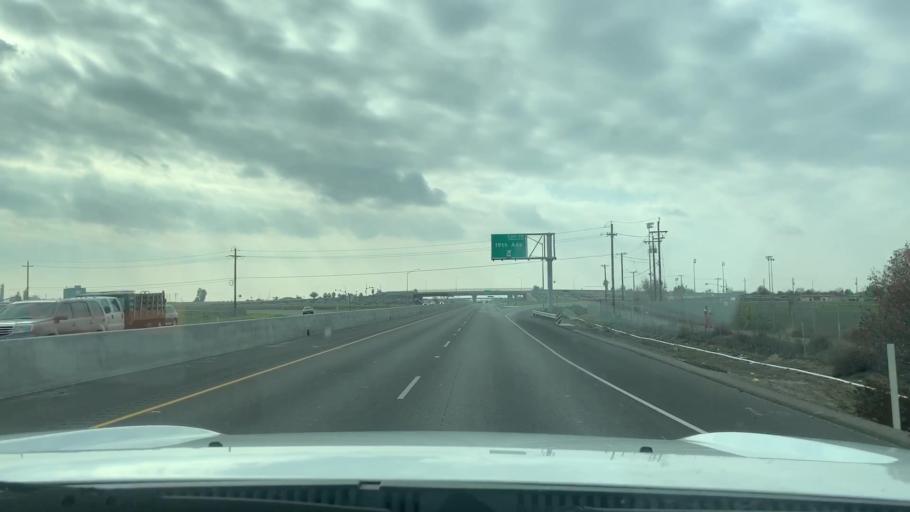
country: US
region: California
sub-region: Kings County
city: Lemoore
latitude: 36.2888
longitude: -119.7934
